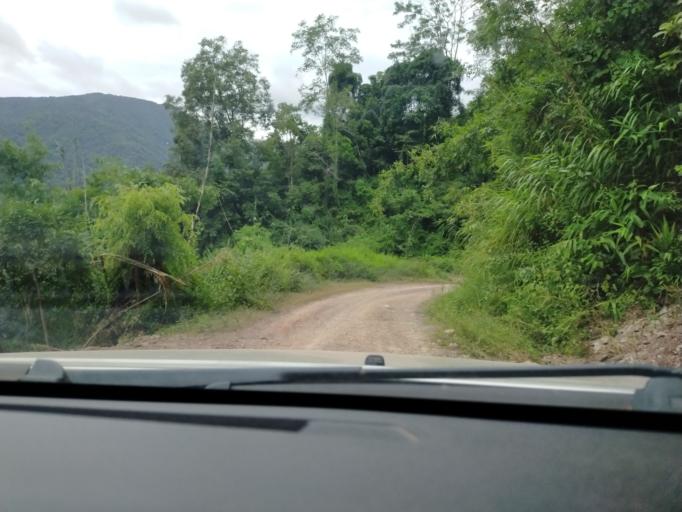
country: TH
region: Nan
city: Chaloem Phra Kiat
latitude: 19.8078
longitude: 101.3622
